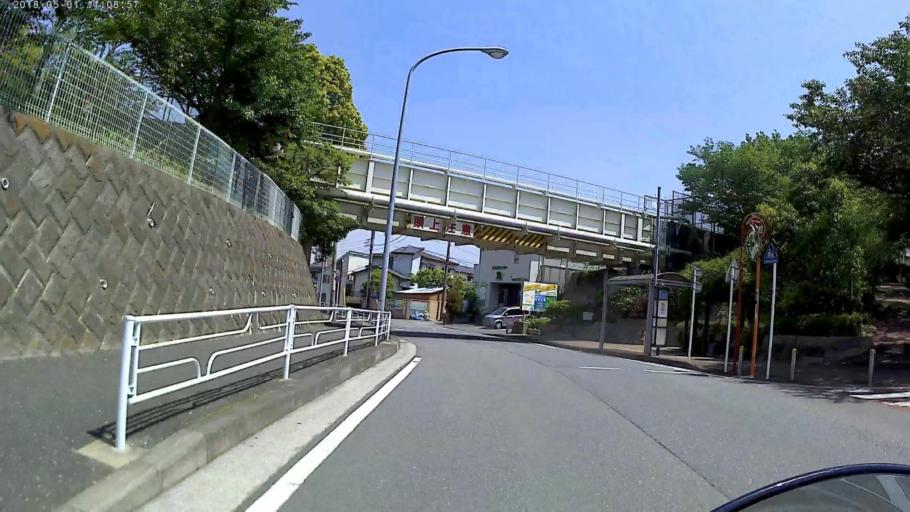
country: JP
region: Kanagawa
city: Minami-rinkan
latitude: 35.4866
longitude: 139.5366
